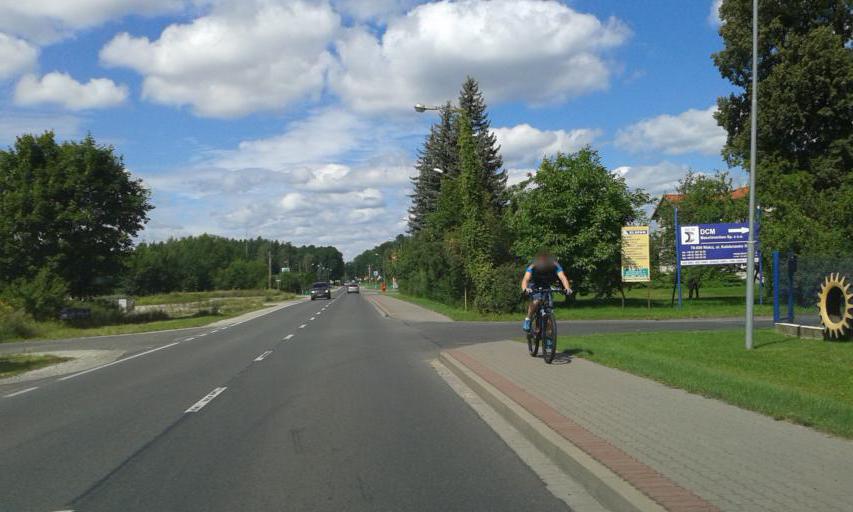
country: PL
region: West Pomeranian Voivodeship
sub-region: Powiat walecki
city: Walcz
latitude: 53.2971
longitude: 16.4563
